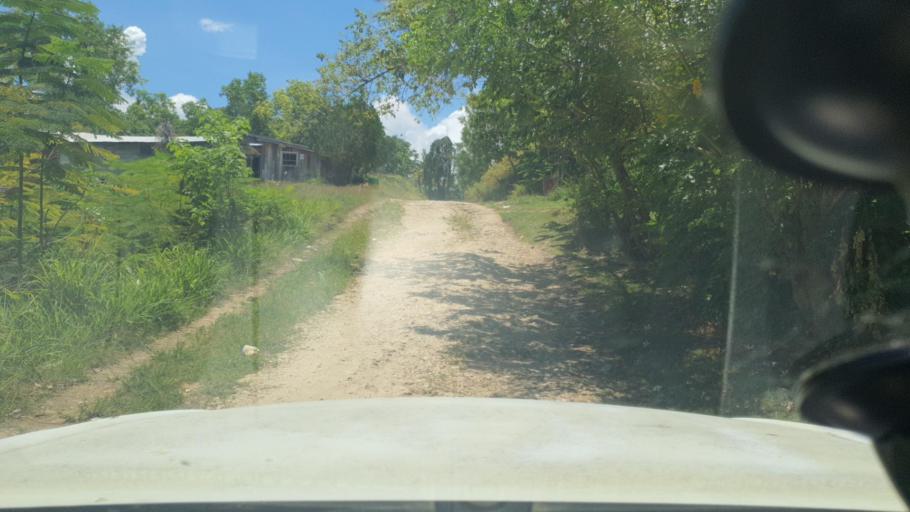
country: SB
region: Guadalcanal
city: Honiara
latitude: -9.4320
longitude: 159.9319
